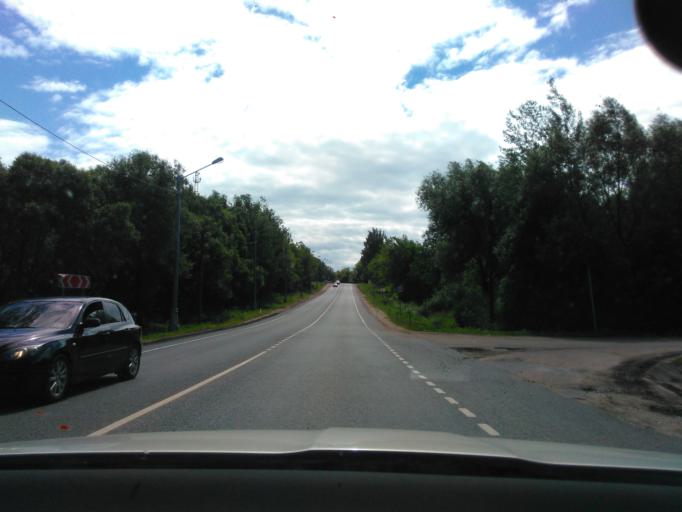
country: RU
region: Moskovskaya
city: Shevlyakovo
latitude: 56.3996
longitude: 36.8641
